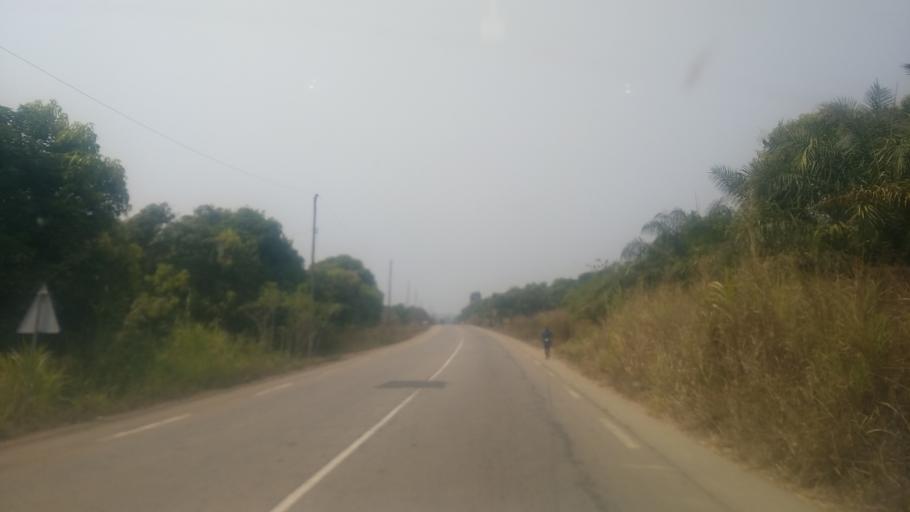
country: CM
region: Centre
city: Bafia
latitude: 4.8311
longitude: 11.0546
